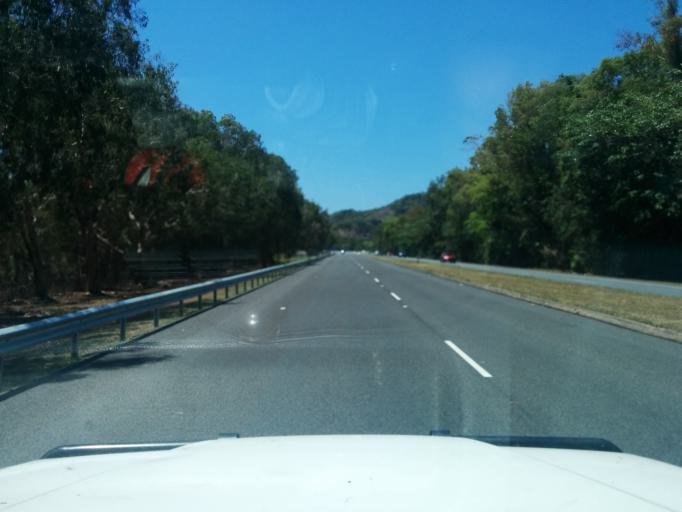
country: AU
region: Queensland
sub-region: Cairns
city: Redlynch
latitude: -16.8793
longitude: 145.7450
